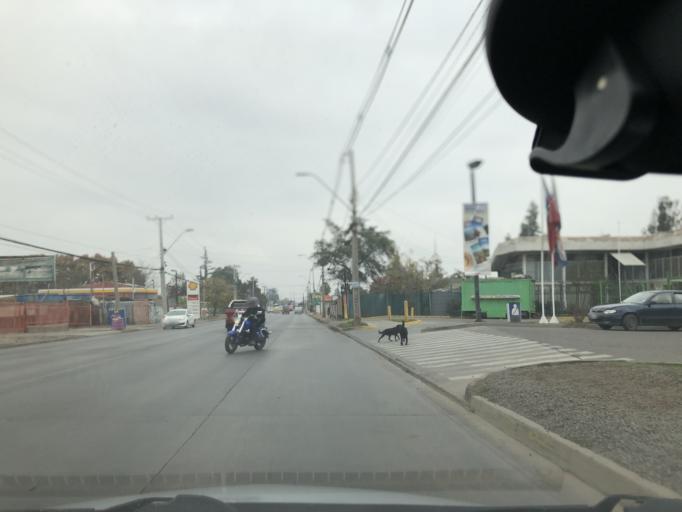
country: CL
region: Santiago Metropolitan
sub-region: Provincia de Santiago
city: La Pintana
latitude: -33.5826
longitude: -70.6064
